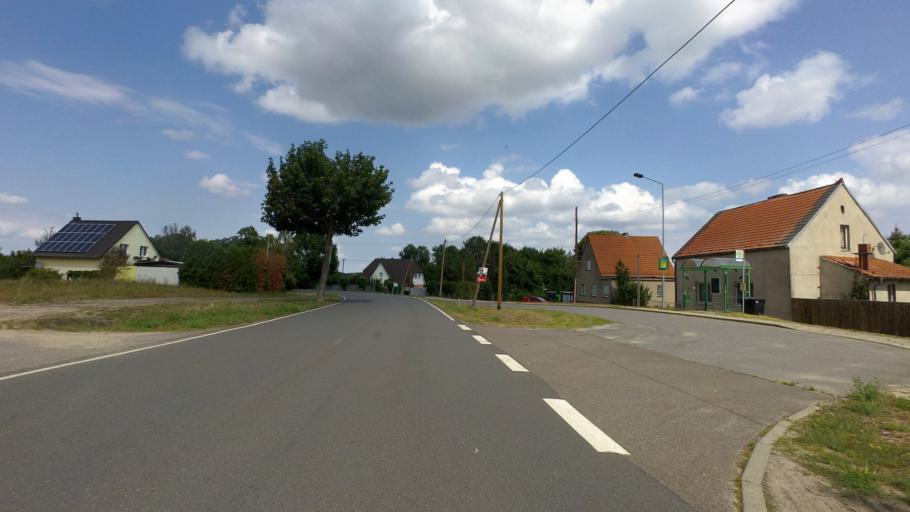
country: DE
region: Brandenburg
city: Teupitz
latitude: 52.1587
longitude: 13.5873
